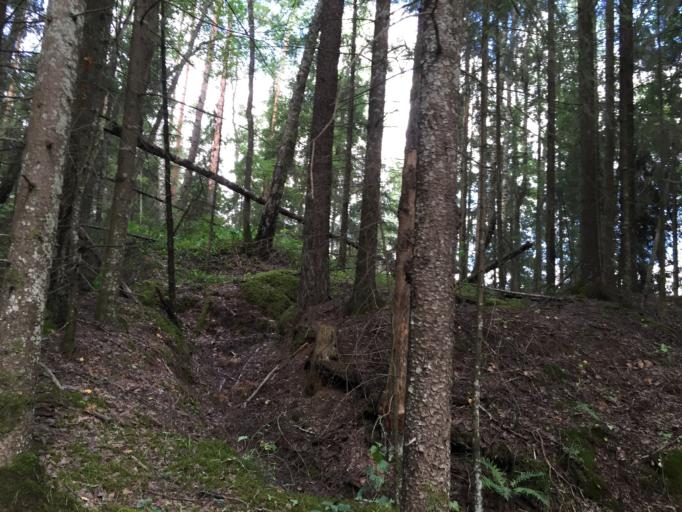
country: LV
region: Ropazu
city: Ropazi
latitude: 56.9180
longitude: 24.7417
